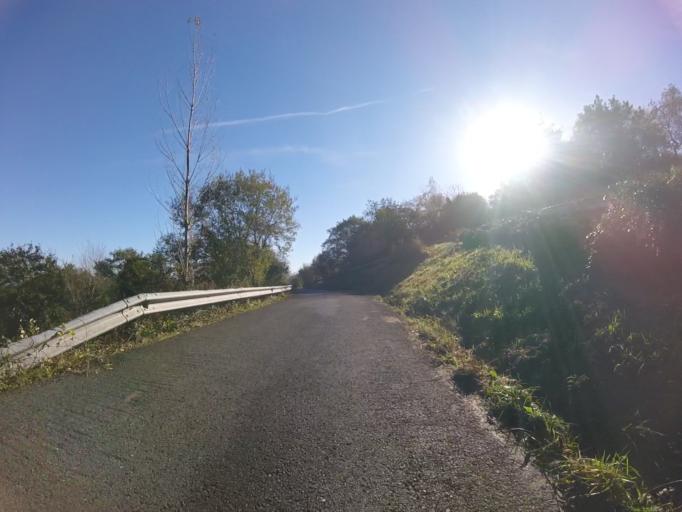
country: ES
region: Basque Country
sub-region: Provincia de Guipuzcoa
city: Usurbil
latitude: 43.2956
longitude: -2.0514
